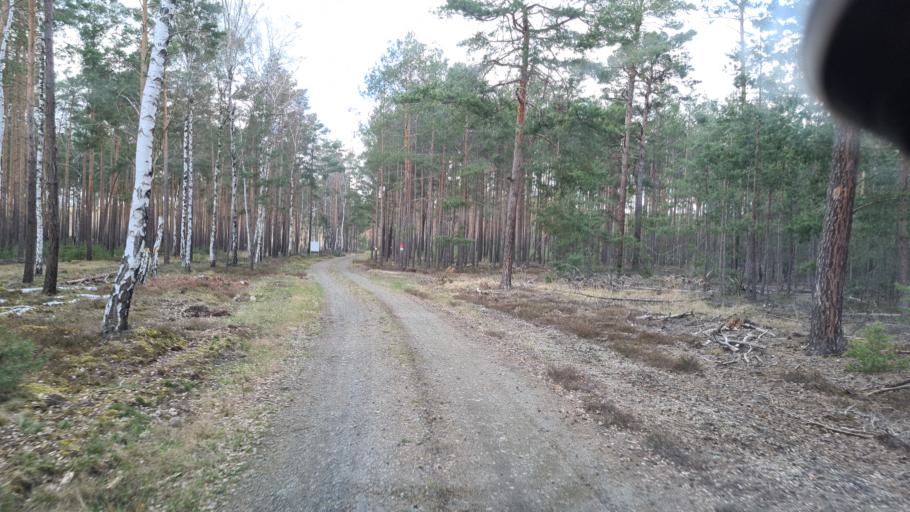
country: DE
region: Brandenburg
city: Schonborn
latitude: 51.6512
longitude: 13.4748
